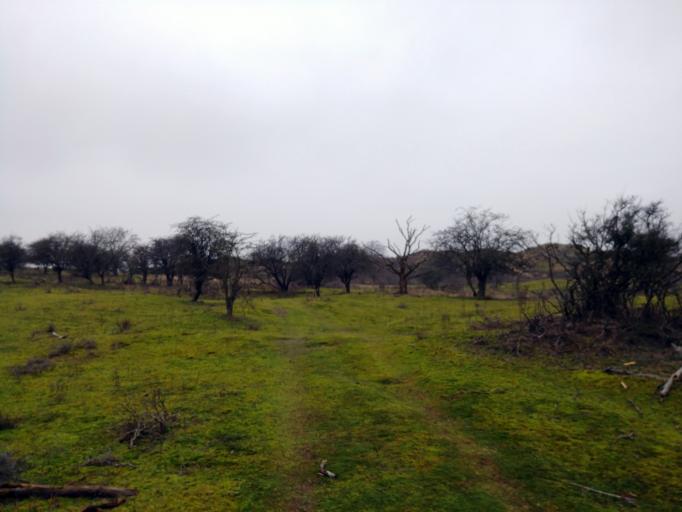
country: NL
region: North Holland
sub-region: Gemeente Zandvoort
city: Zandvoort
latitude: 52.3210
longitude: 4.5384
